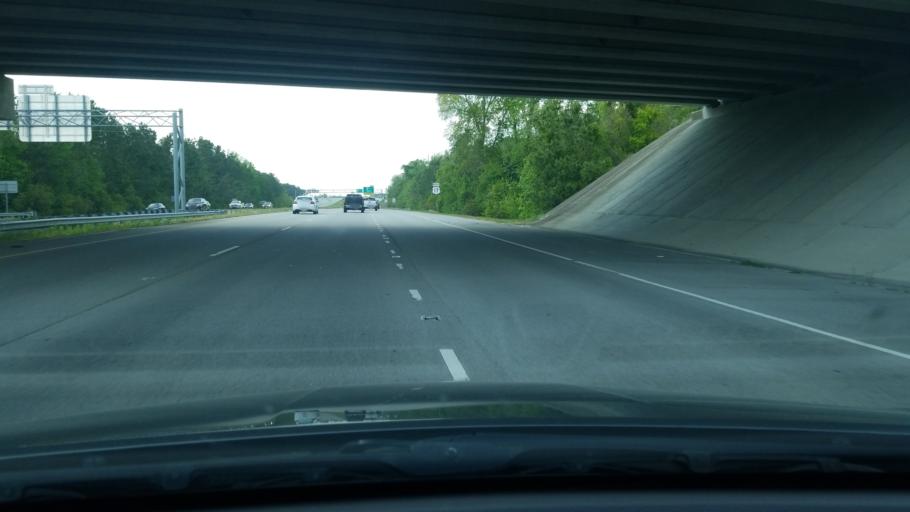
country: US
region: North Carolina
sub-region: Onslow County
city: Jacksonville
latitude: 34.7607
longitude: -77.3942
